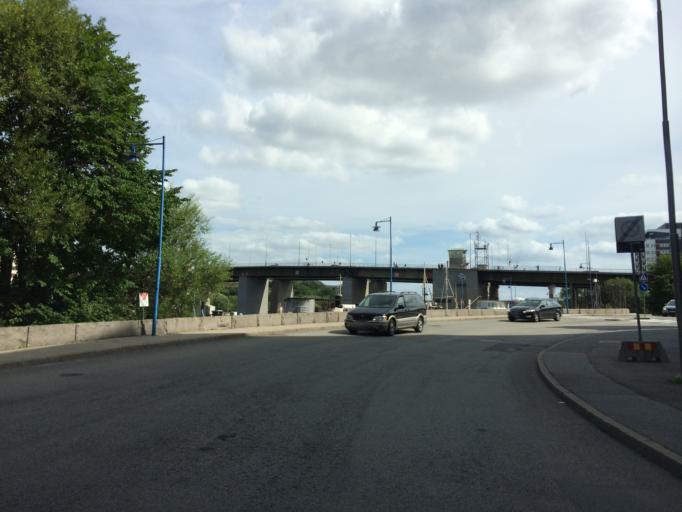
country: SE
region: Stockholm
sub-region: Stockholms Kommun
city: Arsta
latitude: 59.3139
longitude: 18.0282
